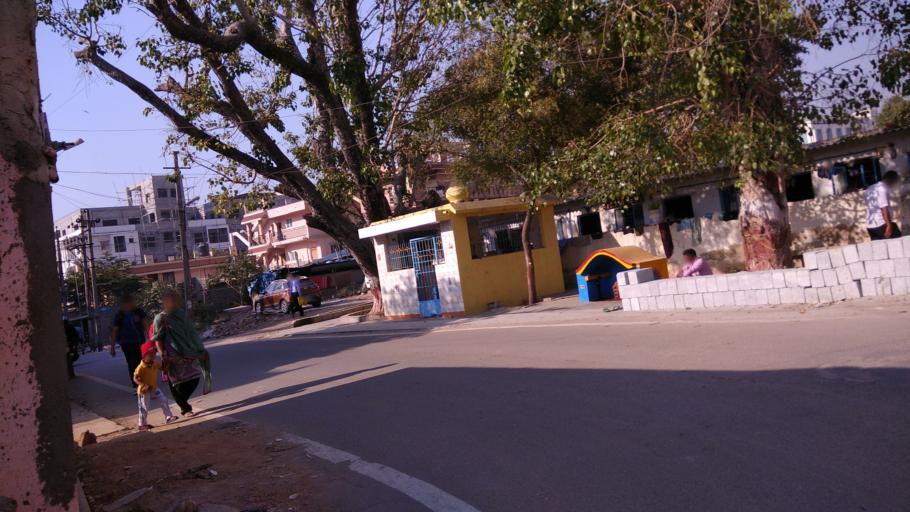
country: IN
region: Karnataka
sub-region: Bangalore Rural
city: Hoskote
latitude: 12.9779
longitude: 77.7336
